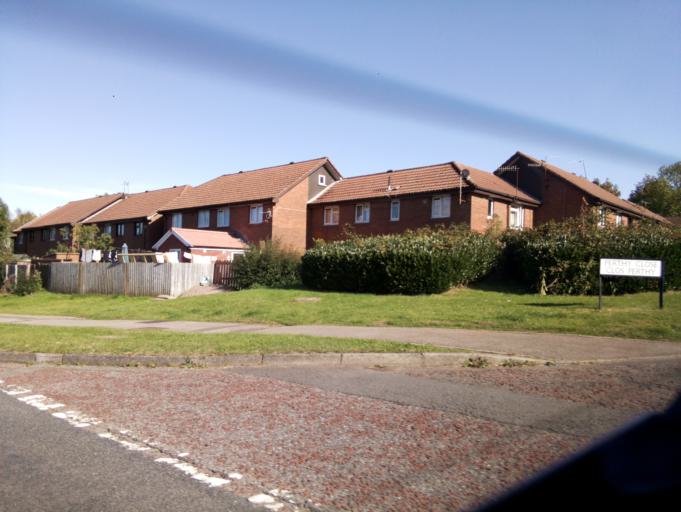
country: GB
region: Wales
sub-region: Torfaen County Borough
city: Cwmbran
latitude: 51.6364
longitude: -3.0440
